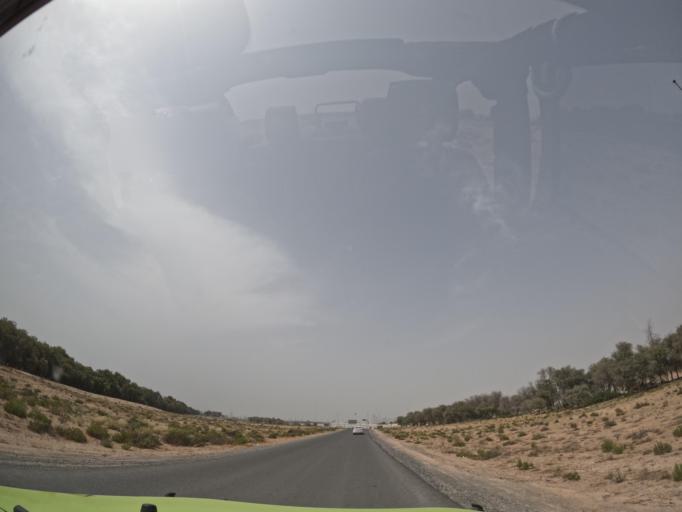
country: AE
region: Dubai
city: Dubai
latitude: 25.1448
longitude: 55.3405
